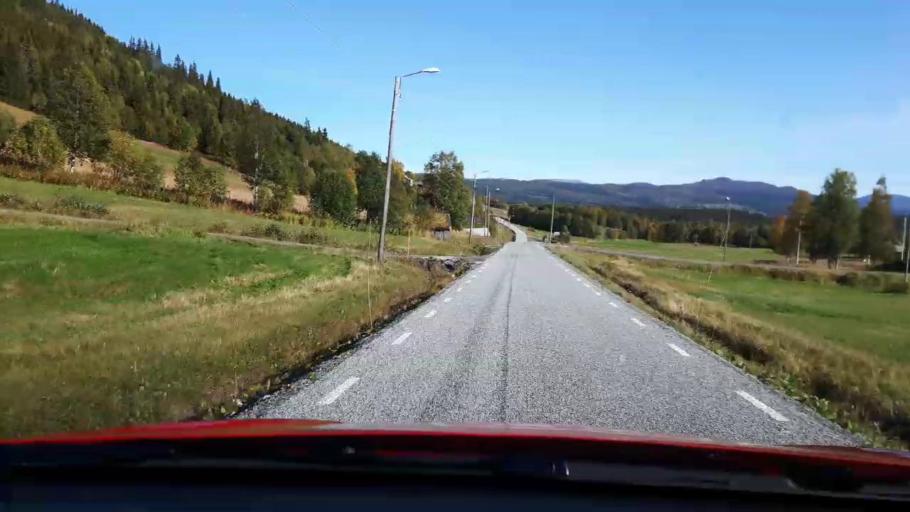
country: NO
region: Nord-Trondelag
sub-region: Royrvik
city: Royrvik
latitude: 64.7289
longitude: 13.9492
